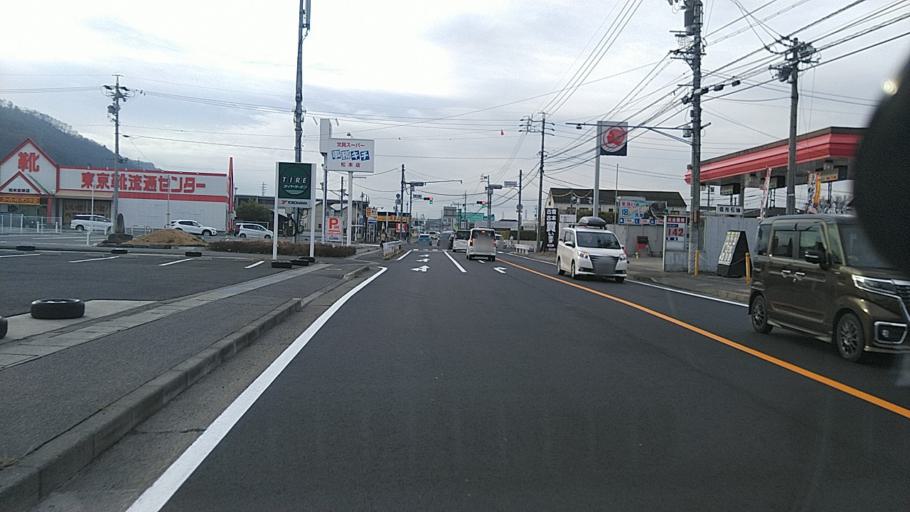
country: JP
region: Nagano
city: Matsumoto
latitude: 36.2145
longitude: 137.9796
